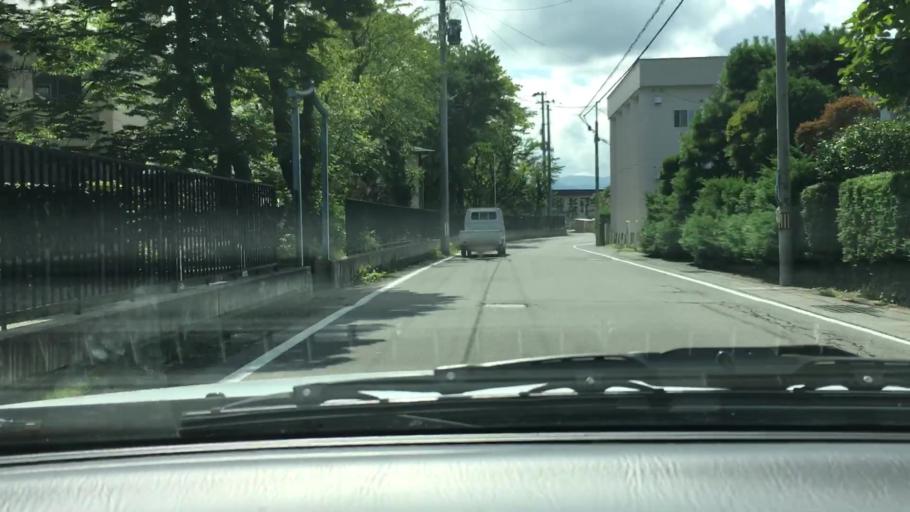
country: JP
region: Aomori
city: Hirosaki
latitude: 40.5889
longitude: 140.4706
